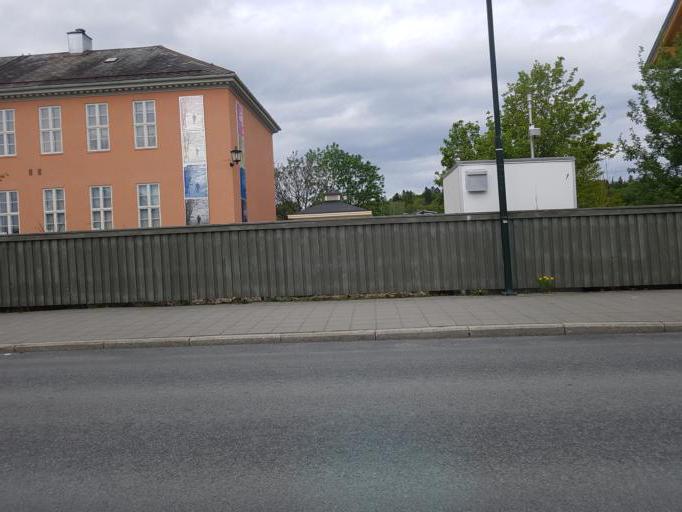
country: NO
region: Nord-Trondelag
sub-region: Levanger
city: Levanger
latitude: 63.7441
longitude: 11.2927
